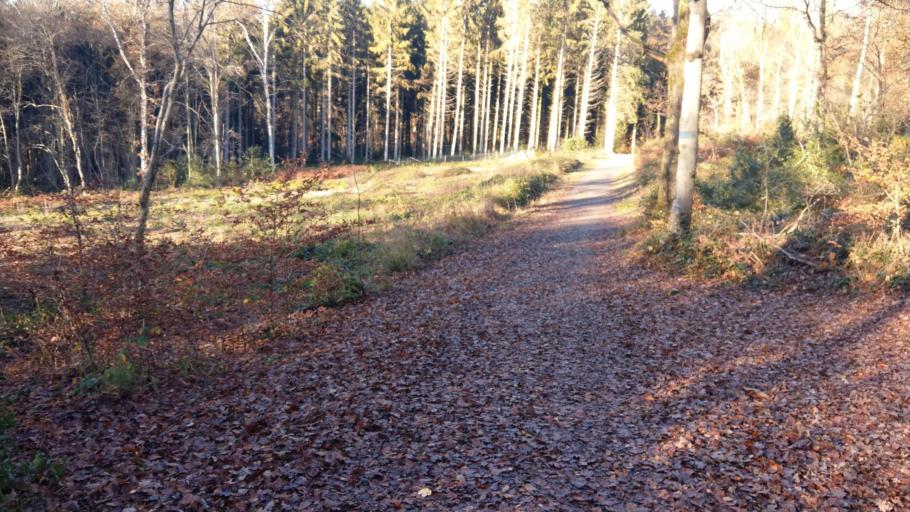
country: BE
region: Wallonia
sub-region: Province de Liege
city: La Calamine
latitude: 50.7317
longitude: 6.0105
